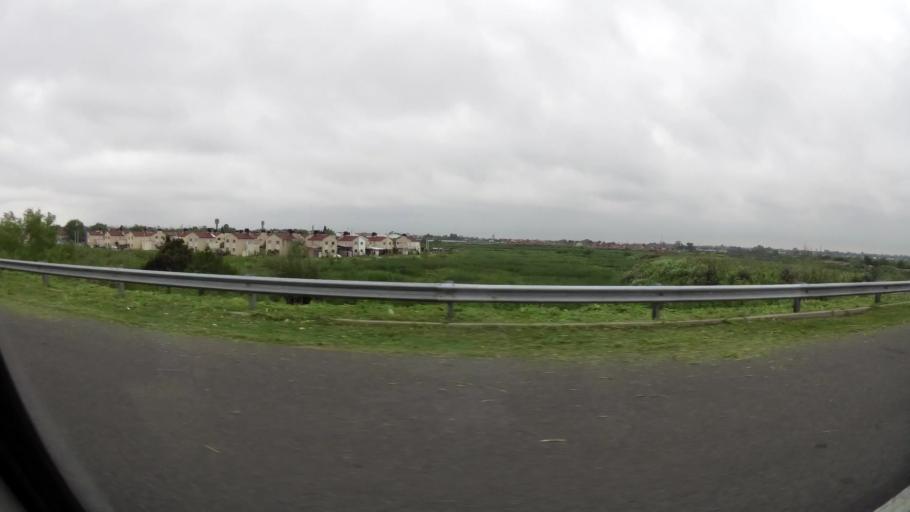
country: AR
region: Buenos Aires
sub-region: Partido de La Plata
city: La Plata
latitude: -34.8737
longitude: -57.9752
